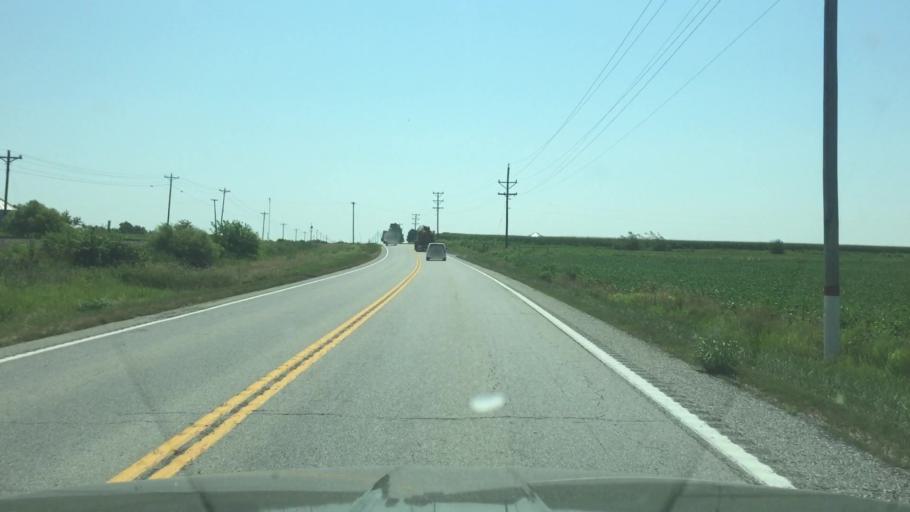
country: US
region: Missouri
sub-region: Moniteau County
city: Tipton
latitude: 38.6661
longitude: -92.8366
